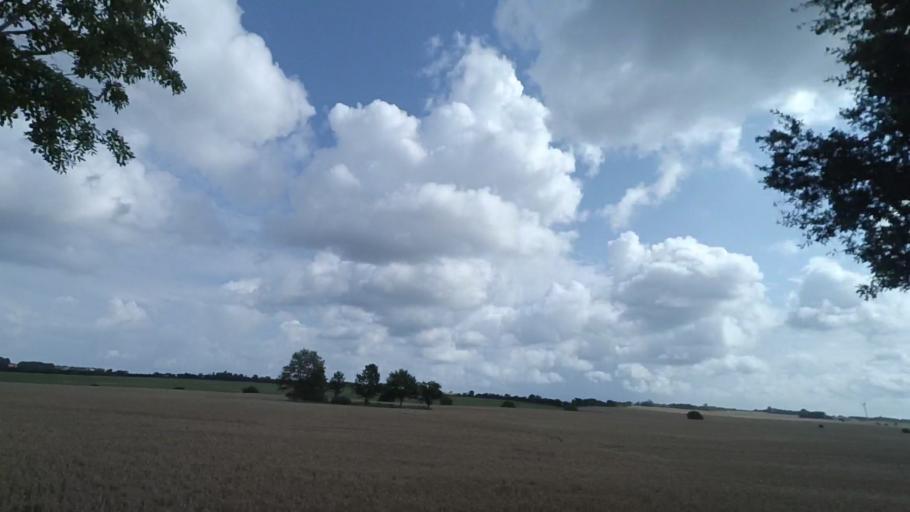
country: DK
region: Central Jutland
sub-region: Norddjurs Kommune
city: Auning
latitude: 56.4956
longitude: 10.4406
